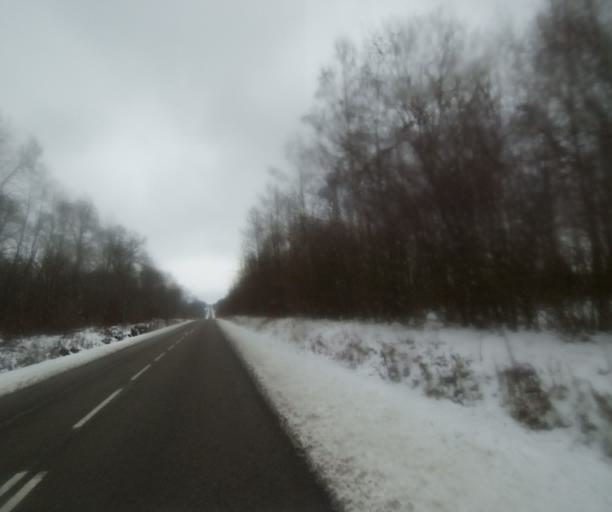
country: FR
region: Champagne-Ardenne
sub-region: Departement de la Haute-Marne
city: Laneuville-a-Remy
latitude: 48.4866
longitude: 4.8289
